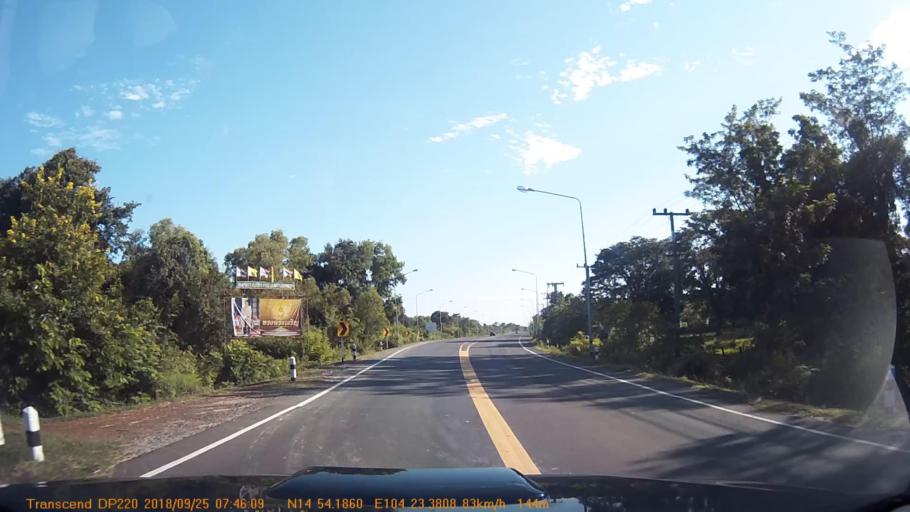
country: TH
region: Sisaket
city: Phayu
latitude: 14.9033
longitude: 104.3897
